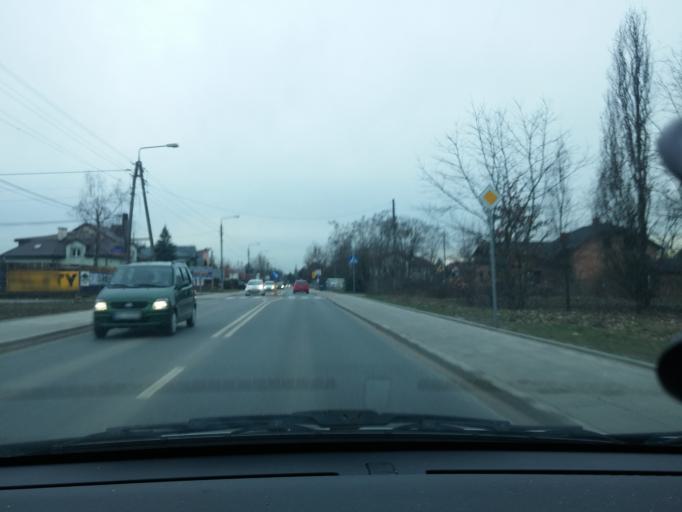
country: PL
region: Masovian Voivodeship
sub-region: Warszawa
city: Wawer
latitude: 52.2016
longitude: 21.1518
